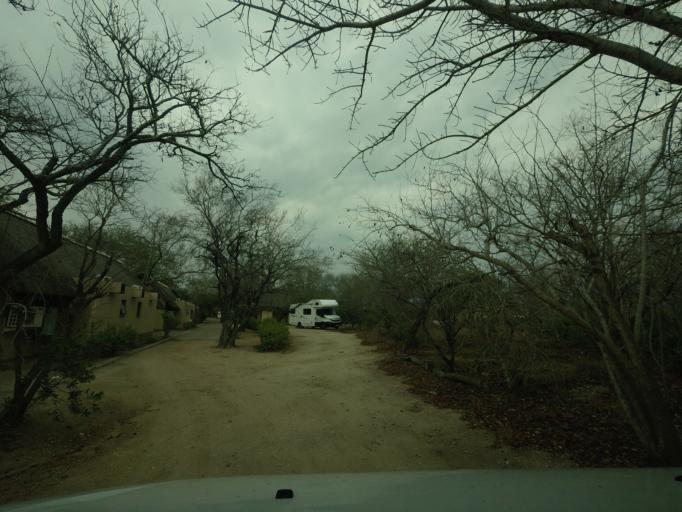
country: ZA
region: Limpopo
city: Thulamahashi
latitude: -24.4745
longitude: 31.3907
